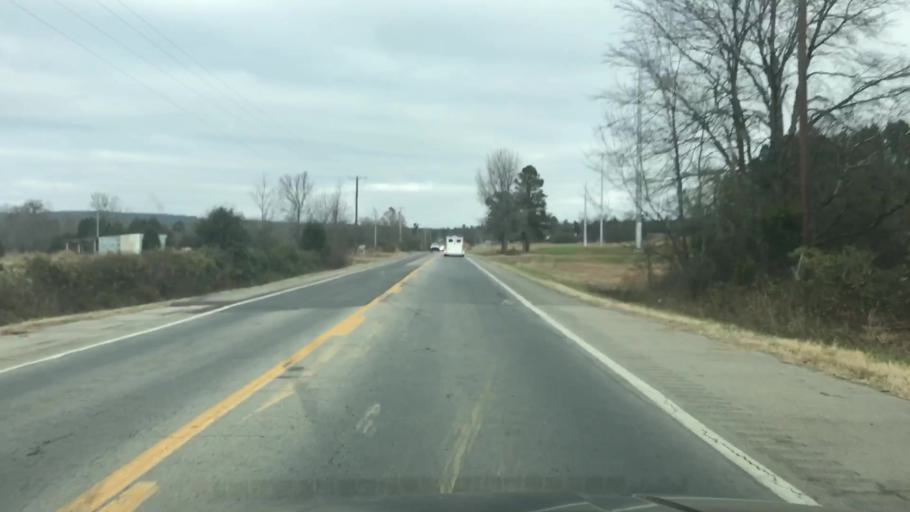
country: US
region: Arkansas
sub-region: Scott County
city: Waldron
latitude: 34.9425
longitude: -94.1028
